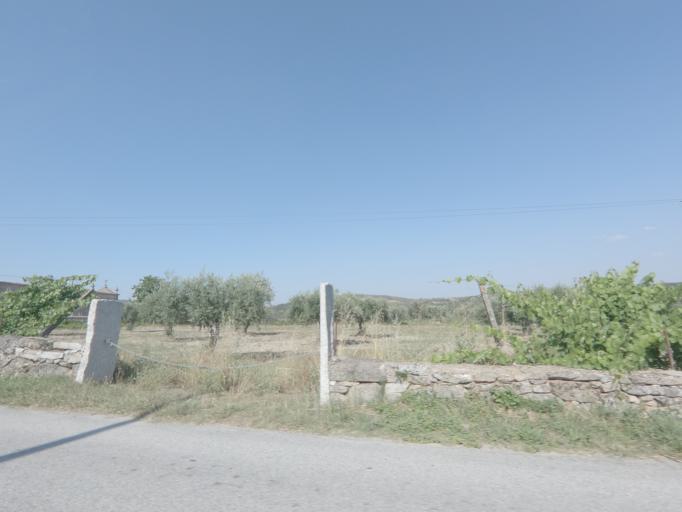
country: PT
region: Viseu
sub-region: Moimenta da Beira
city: Moimenta da Beira
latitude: 40.9726
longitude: -7.5913
